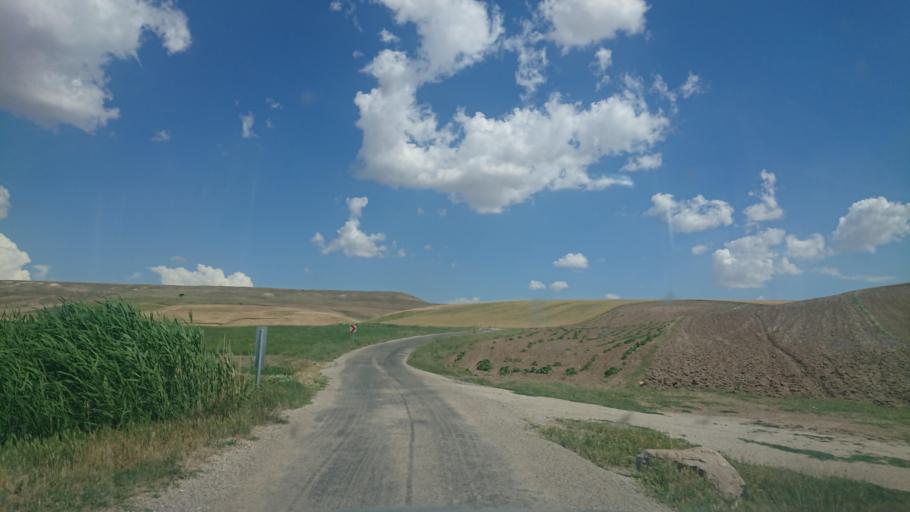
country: TR
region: Aksaray
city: Agacoren
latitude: 38.8148
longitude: 33.7970
